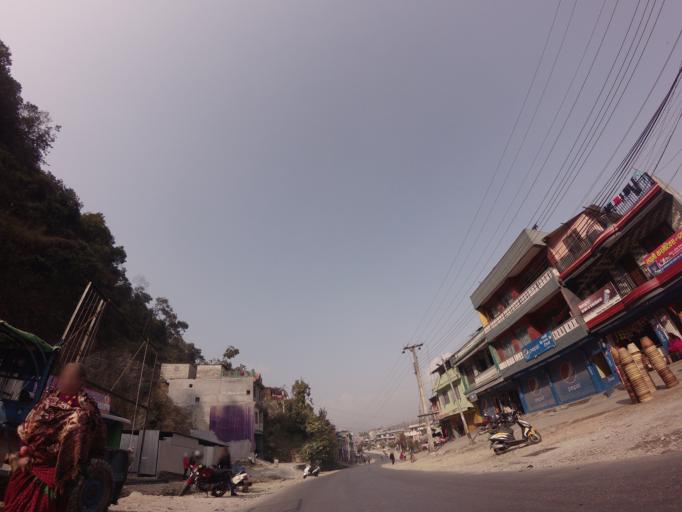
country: NP
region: Western Region
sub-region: Gandaki Zone
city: Pokhara
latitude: 28.2441
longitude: 83.9825
